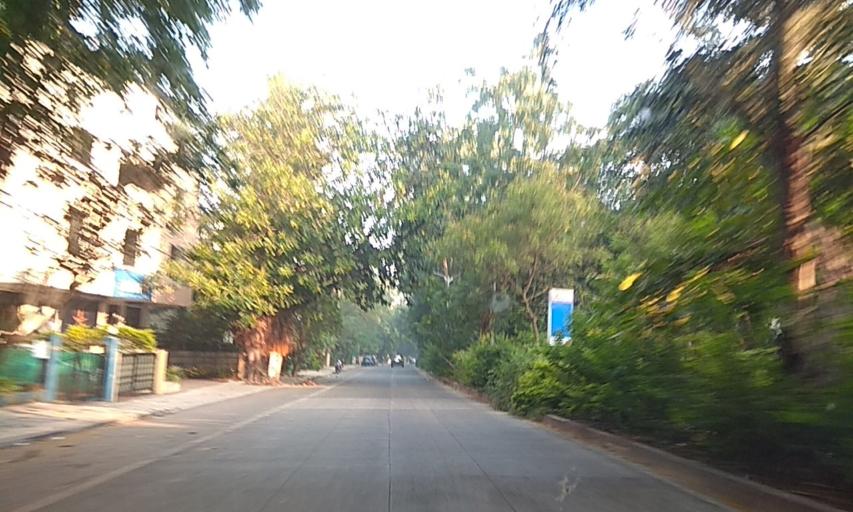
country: IN
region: Maharashtra
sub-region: Pune Division
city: Shivaji Nagar
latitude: 18.5411
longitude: 73.8175
